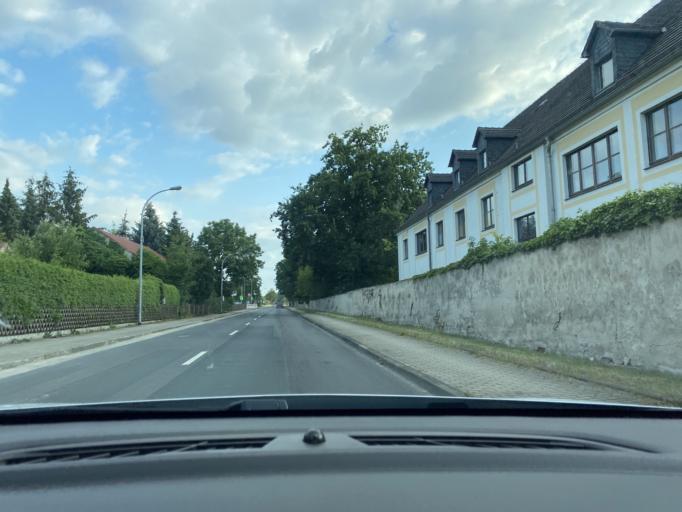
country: DE
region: Saxony
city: Konigswartha
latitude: 51.3073
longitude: 14.3277
